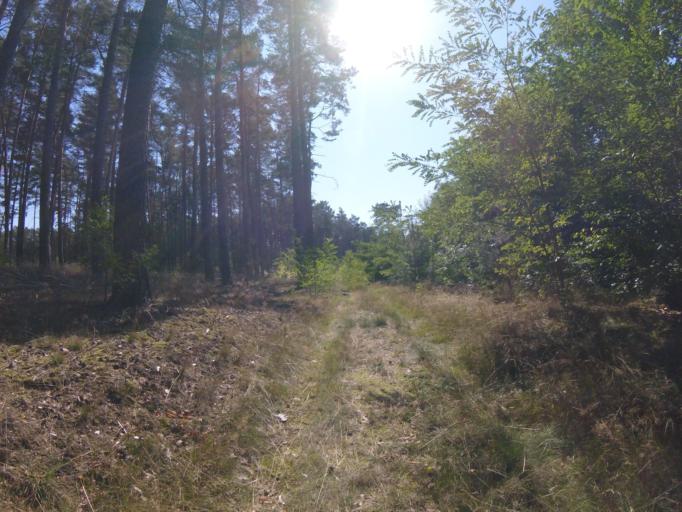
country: DE
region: Brandenburg
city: Bestensee
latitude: 52.2749
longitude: 13.6775
